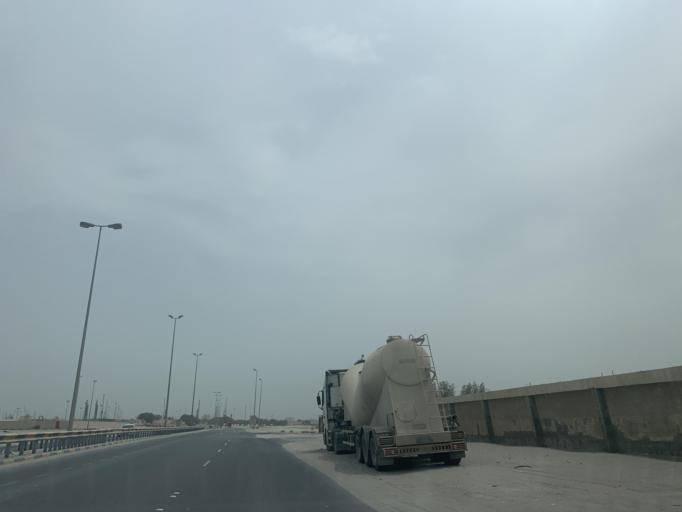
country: BH
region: Muharraq
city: Al Hadd
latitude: 26.2044
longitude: 50.6600
